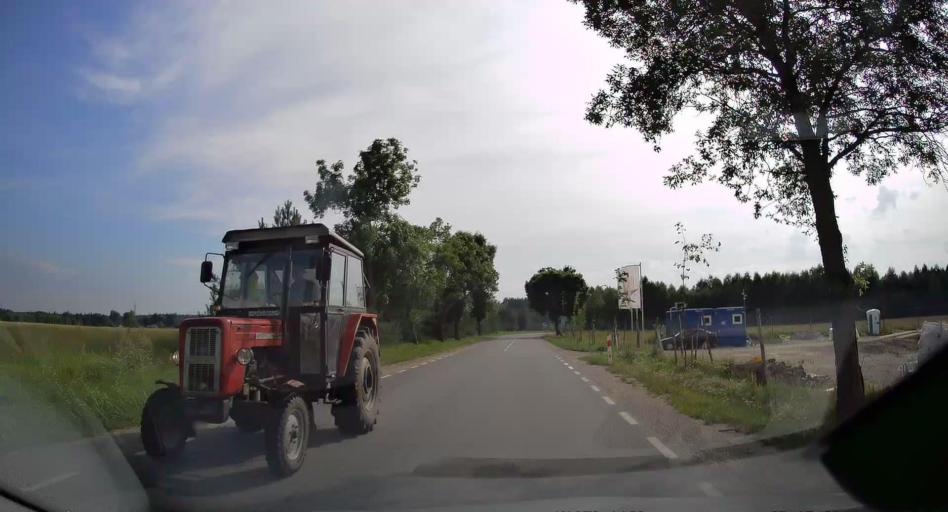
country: PL
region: Lodz Voivodeship
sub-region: Powiat tomaszowski
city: Inowlodz
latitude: 51.5590
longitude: 20.2611
